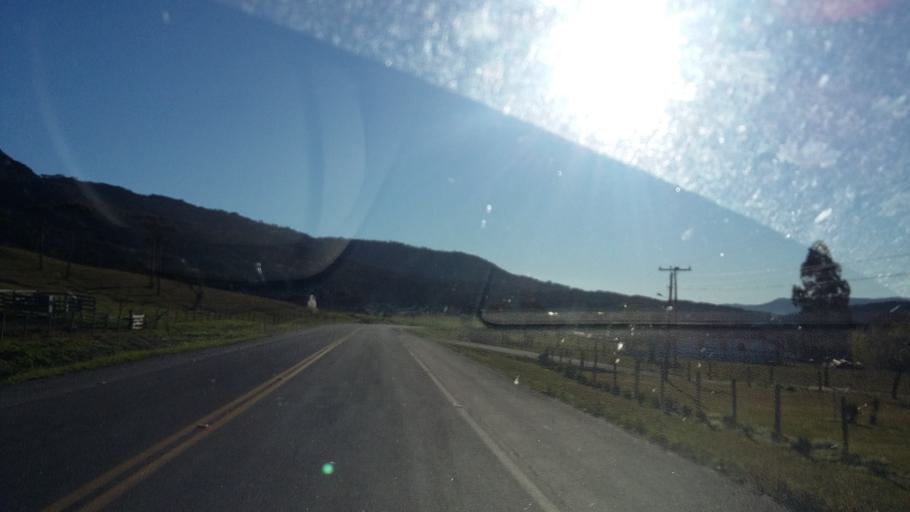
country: BR
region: Santa Catarina
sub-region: Lauro Muller
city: Lauro Muller
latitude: -28.0192
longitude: -49.5166
